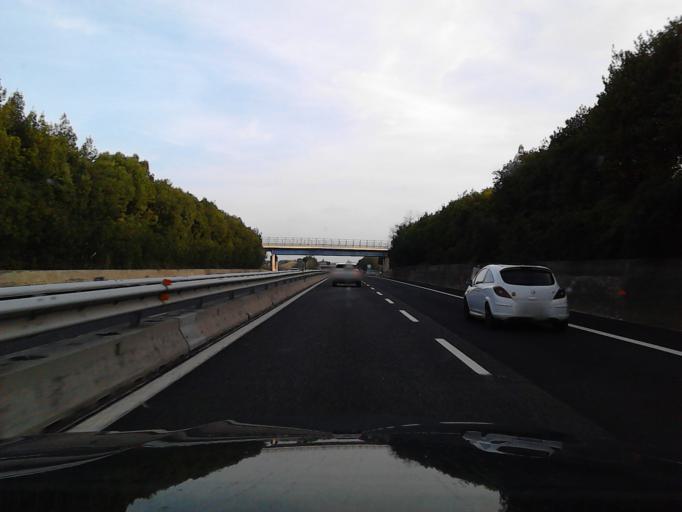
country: IT
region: Abruzzo
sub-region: Provincia di Chieti
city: Ortona
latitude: 42.3249
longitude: 14.3913
